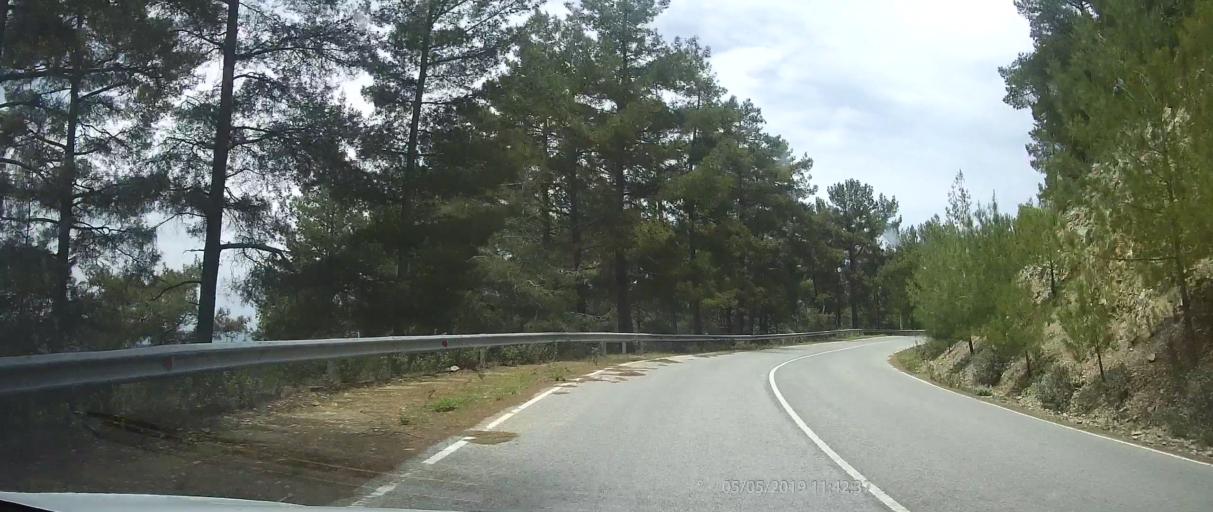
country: CY
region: Lefkosia
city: Kato Pyrgos
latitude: 35.0028
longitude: 32.6709
